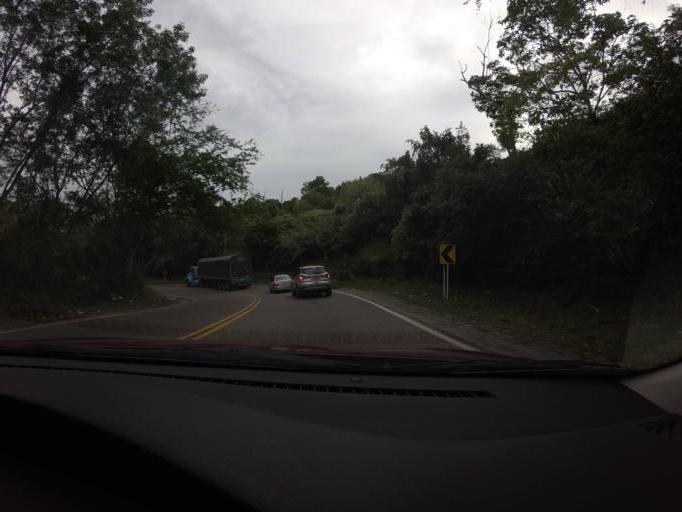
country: CO
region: Cundinamarca
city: Villeta
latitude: 5.0288
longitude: -74.5070
